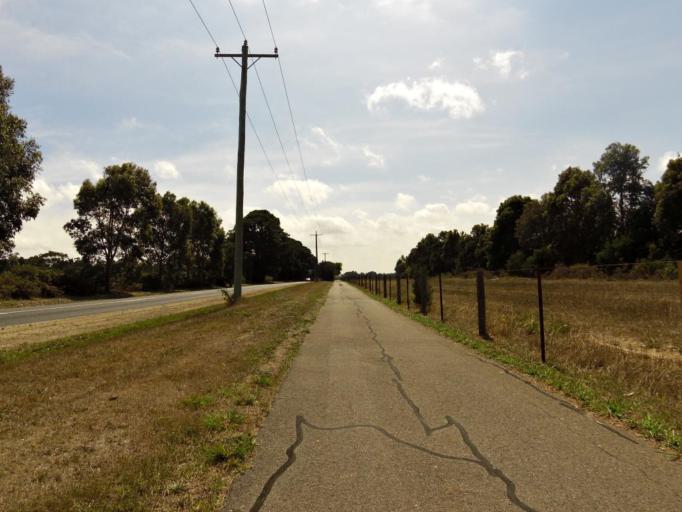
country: AU
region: Victoria
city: Somers
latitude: -38.3738
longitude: 145.1754
